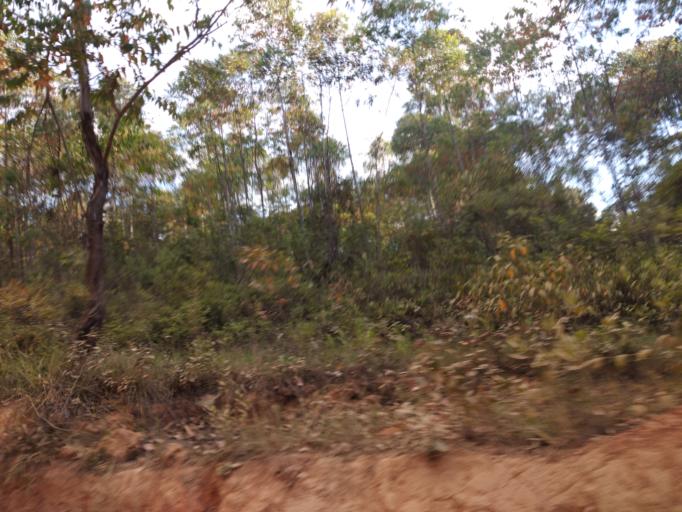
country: BR
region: Minas Gerais
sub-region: Sao Joao Del Rei
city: Sao Joao del Rei
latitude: -20.9060
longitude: -44.2885
